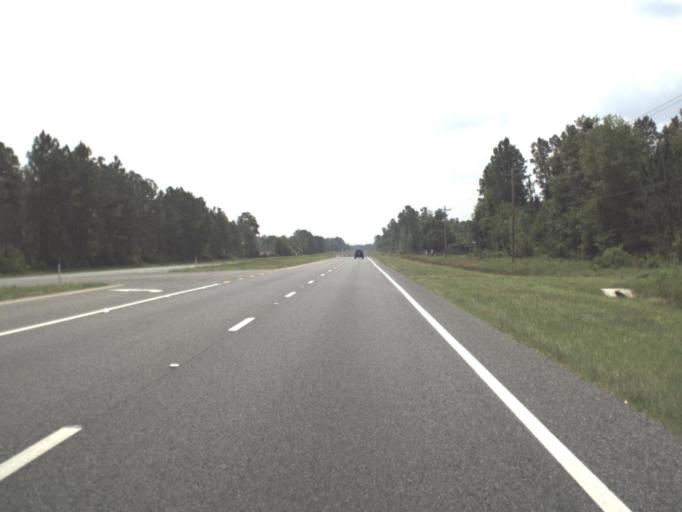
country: US
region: Florida
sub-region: Putnam County
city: East Palatka
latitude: 29.7955
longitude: -81.6515
